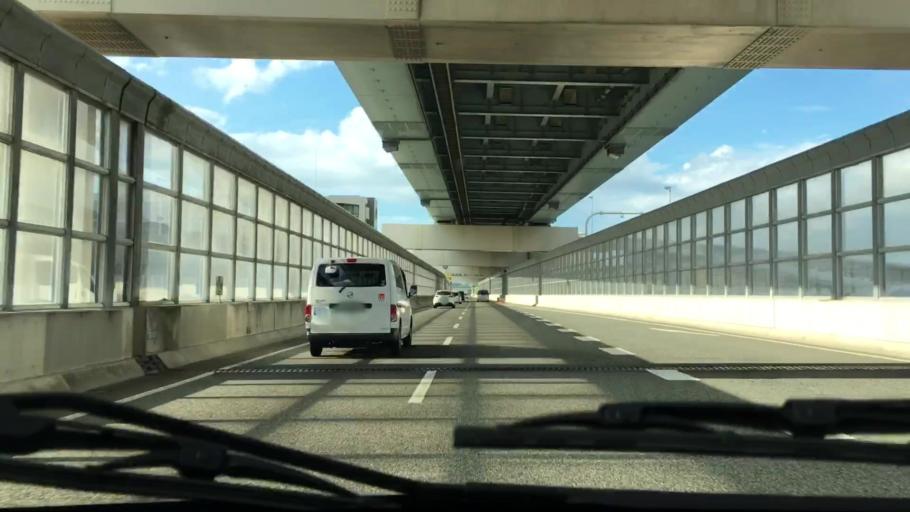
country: JP
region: Fukuoka
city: Fukuoka-shi
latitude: 33.5714
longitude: 130.3168
